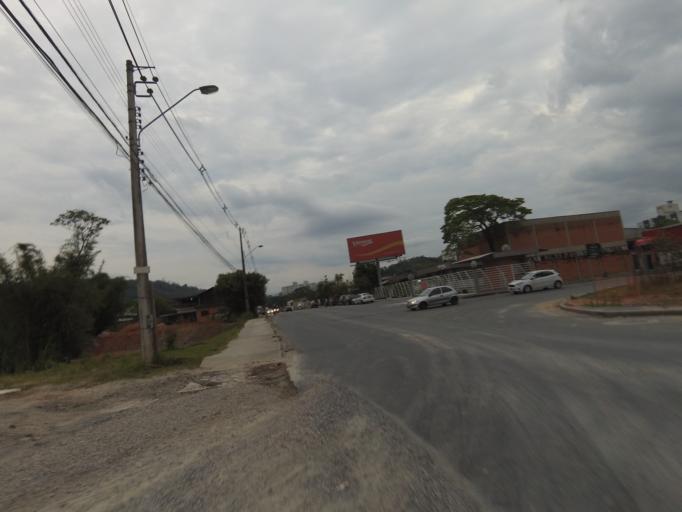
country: BR
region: Santa Catarina
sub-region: Blumenau
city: Blumenau
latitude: -26.8910
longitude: -49.0631
